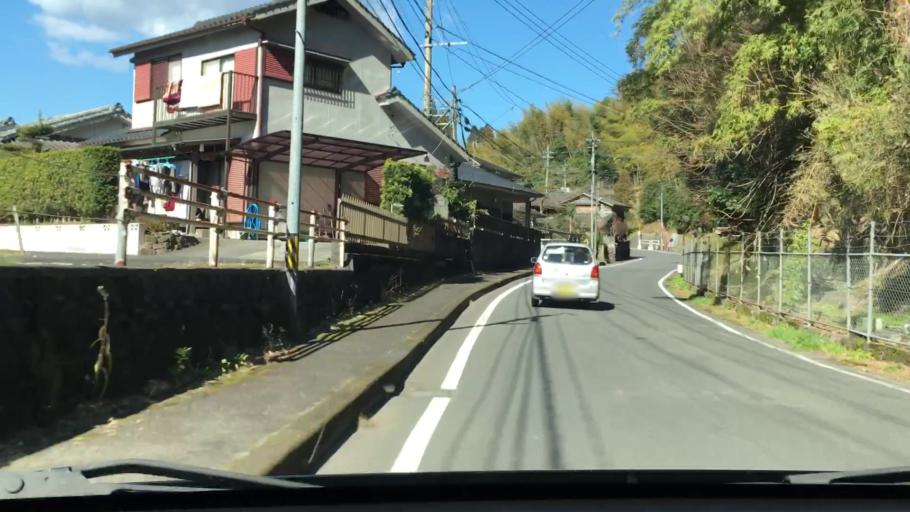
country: JP
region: Kagoshima
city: Ijuin
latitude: 31.6875
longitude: 130.4677
